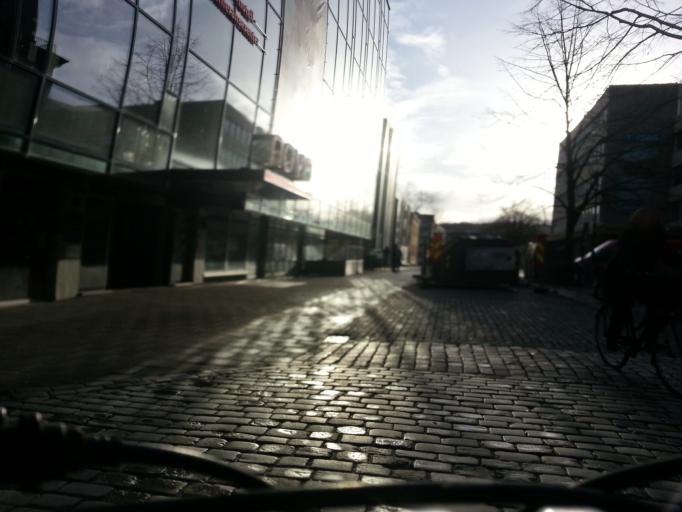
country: NO
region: Sor-Trondelag
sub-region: Trondheim
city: Trondheim
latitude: 63.4326
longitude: 10.4007
